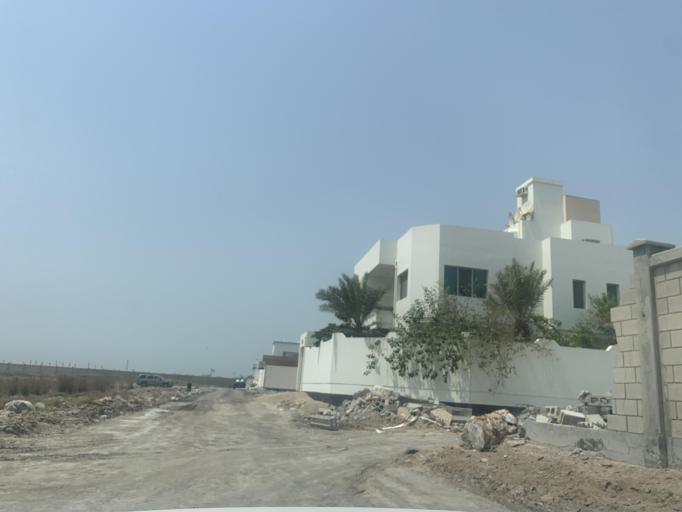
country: BH
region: Central Governorate
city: Madinat Hamad
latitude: 26.1246
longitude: 50.4635
